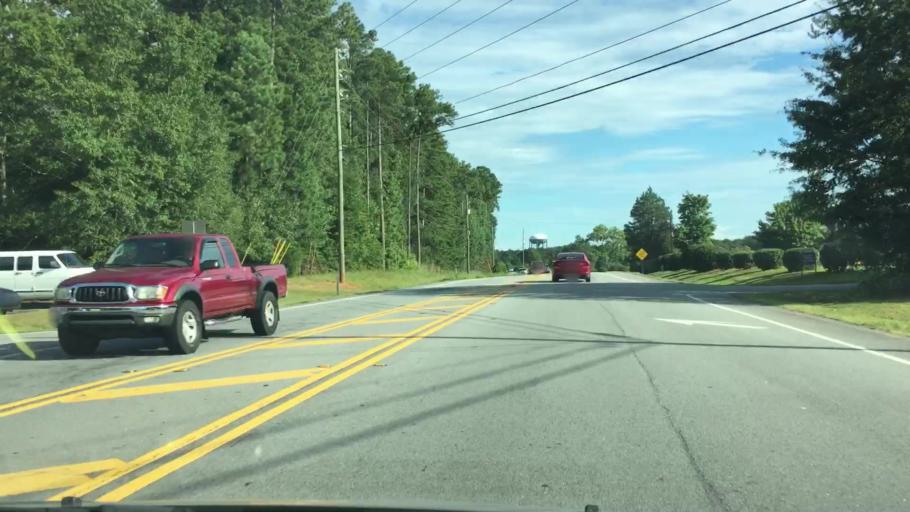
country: US
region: Georgia
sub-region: Henry County
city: Stockbridge
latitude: 33.6189
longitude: -84.2348
